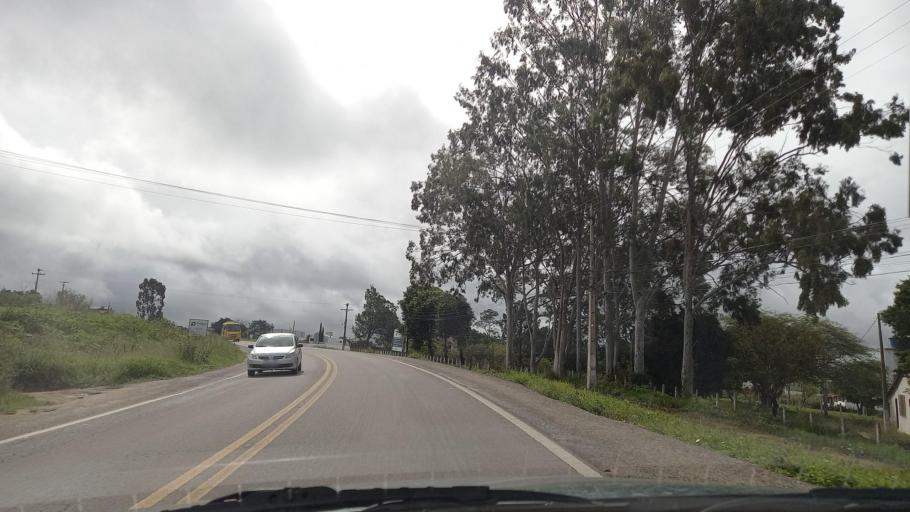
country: BR
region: Pernambuco
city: Garanhuns
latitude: -8.9115
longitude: -36.4933
